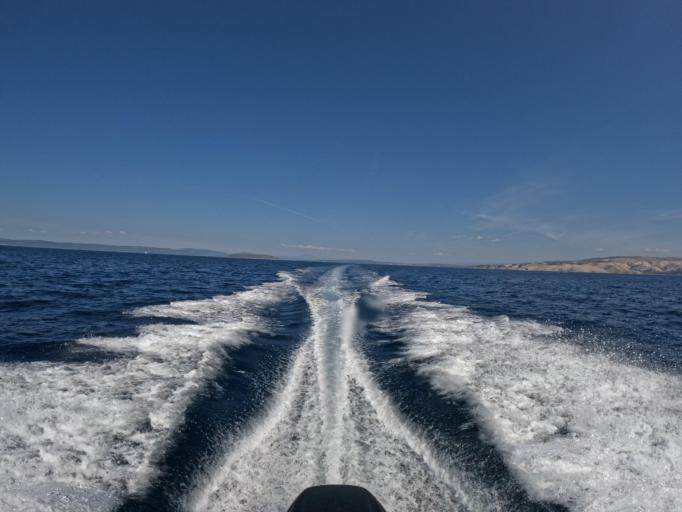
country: HR
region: Primorsko-Goranska
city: Punat
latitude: 44.9029
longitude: 14.6340
